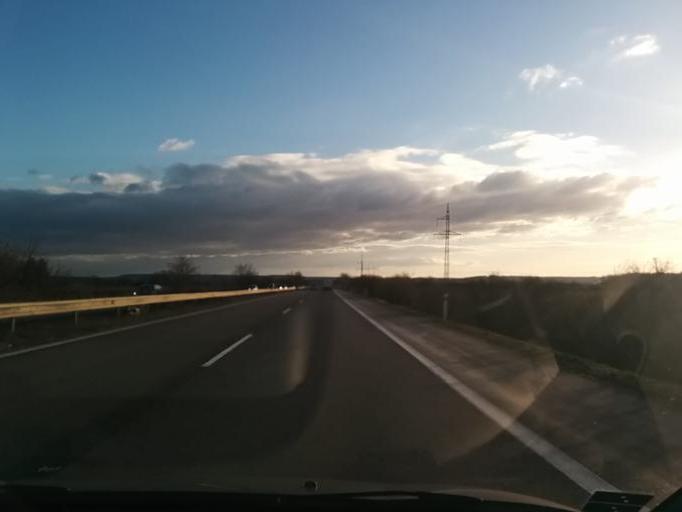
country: SK
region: Trnavsky
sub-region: Okres Trnava
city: Trnava
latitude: 48.3608
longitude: 17.6856
